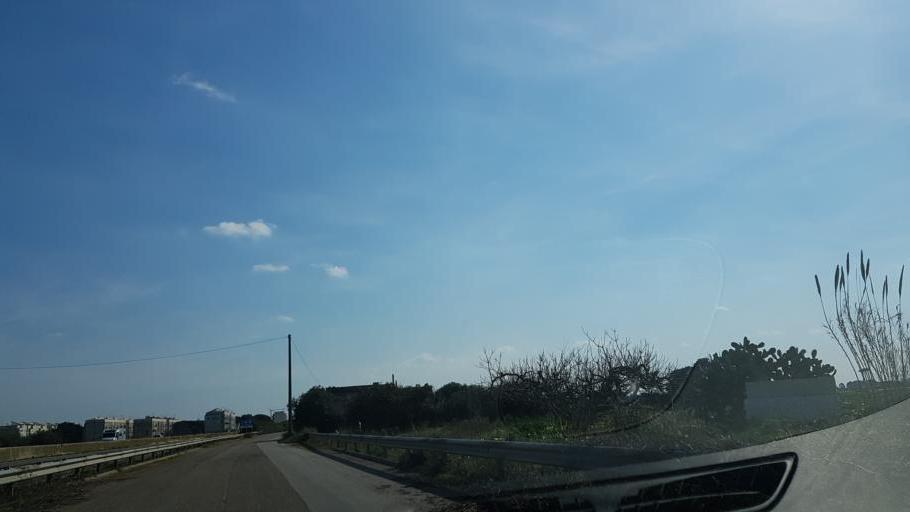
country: IT
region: Apulia
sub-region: Provincia di Brindisi
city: Brindisi
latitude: 40.6521
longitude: 17.9063
